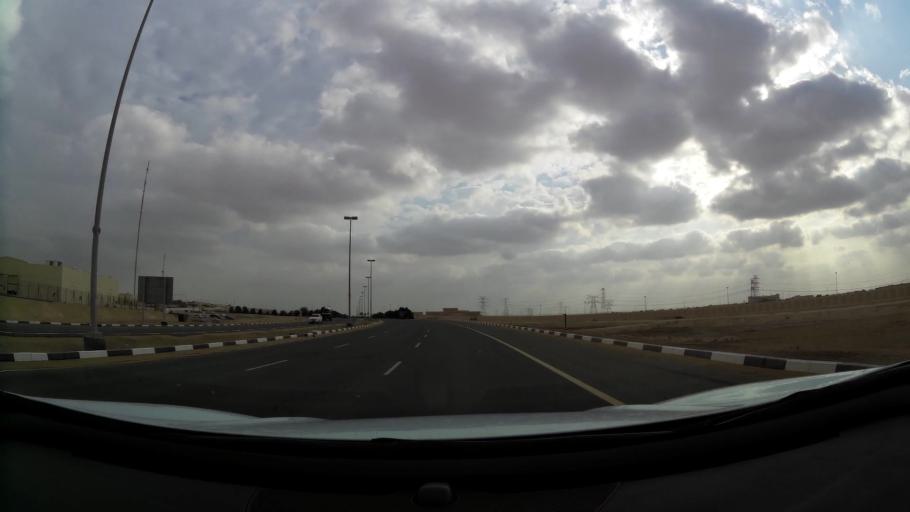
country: AE
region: Abu Dhabi
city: Abu Dhabi
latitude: 24.3415
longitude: 54.5917
